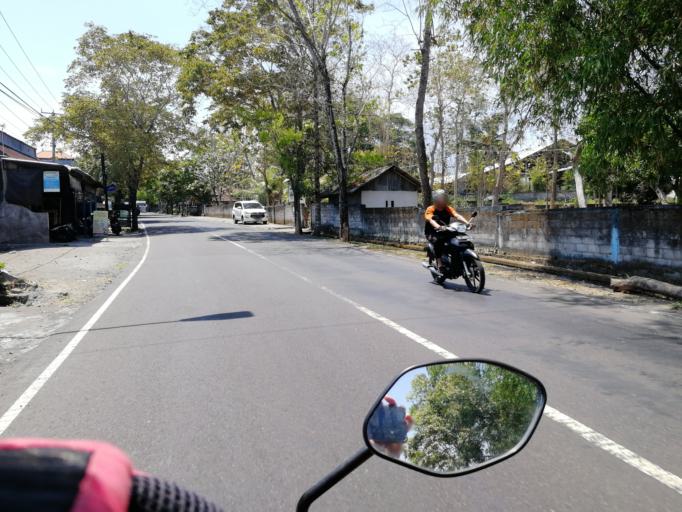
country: ID
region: Bali
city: Banjar Beji
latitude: -8.4492
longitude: 115.5920
